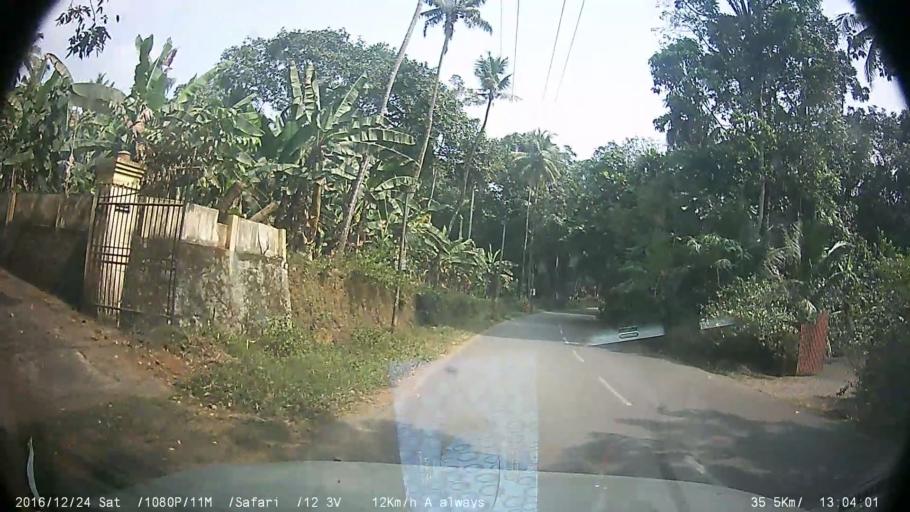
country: IN
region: Kerala
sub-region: Ernakulam
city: Muvattupuzha
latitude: 9.8911
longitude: 76.5924
